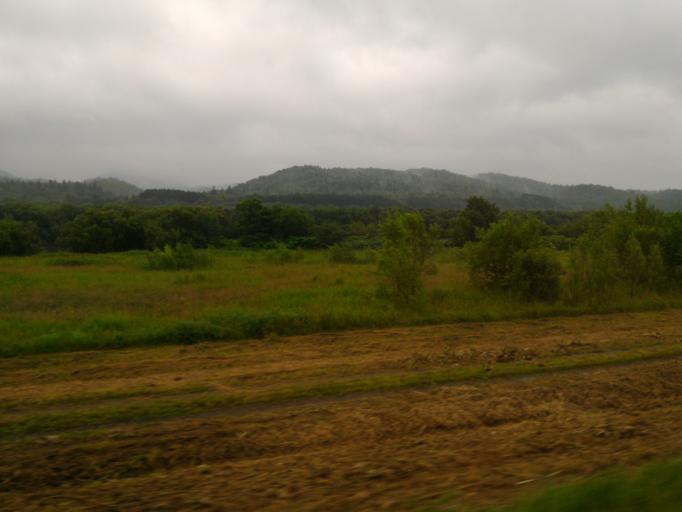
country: JP
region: Hokkaido
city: Nayoro
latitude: 44.7600
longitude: 142.0510
